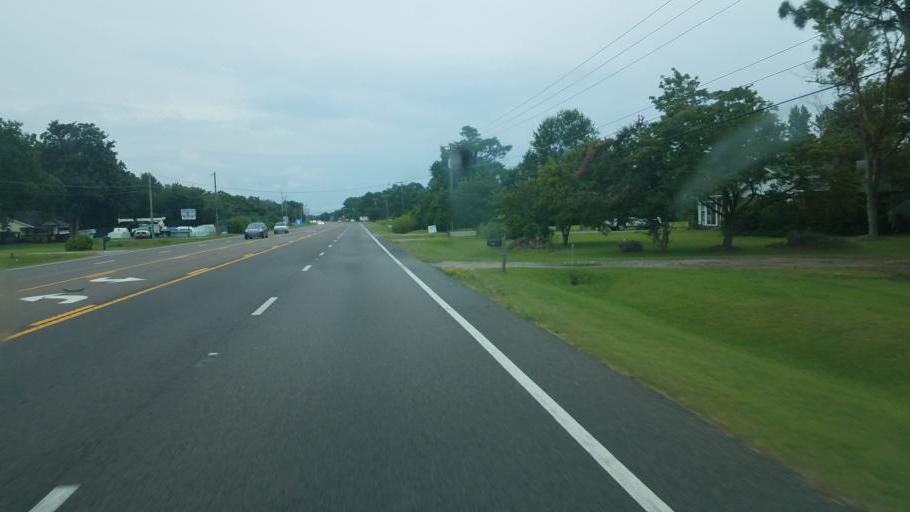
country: US
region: North Carolina
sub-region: Dare County
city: Southern Shores
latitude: 36.1278
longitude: -75.8370
